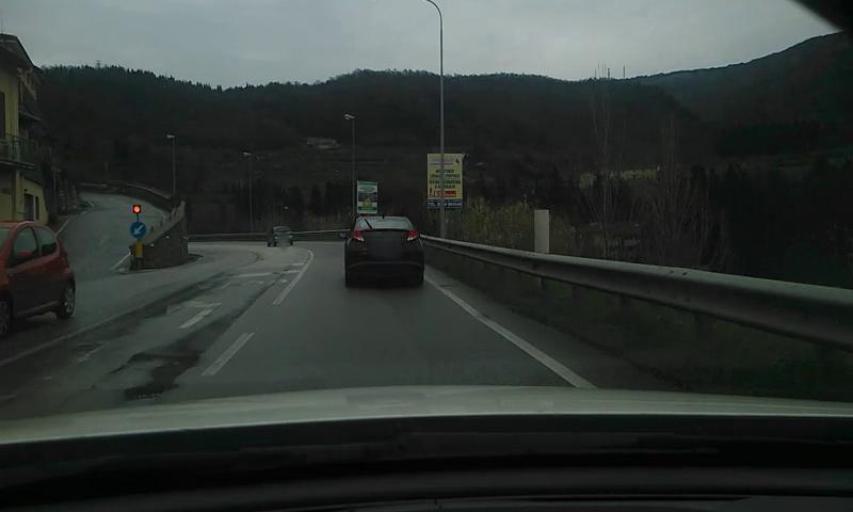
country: IT
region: Tuscany
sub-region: Provincia di Prato
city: Vaiano
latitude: 43.9392
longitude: 11.1279
